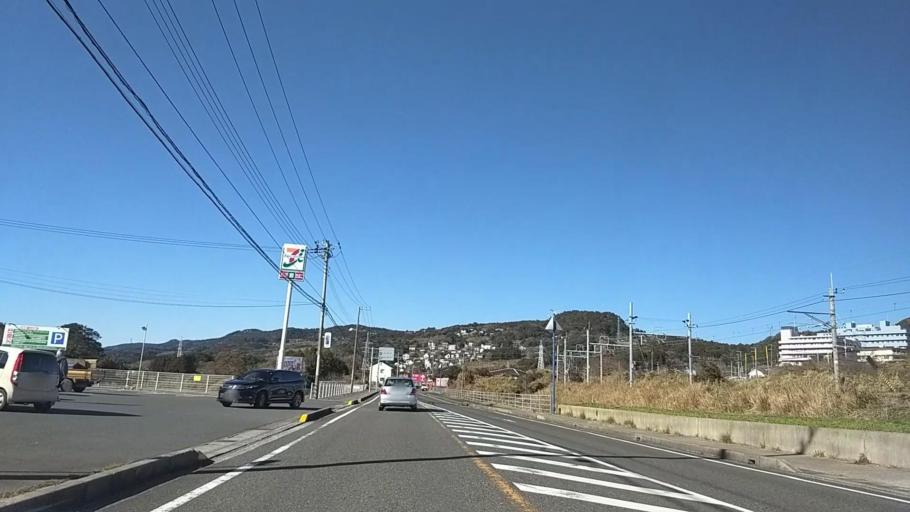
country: JP
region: Chiba
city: Kawaguchi
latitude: 35.0867
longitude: 140.0928
